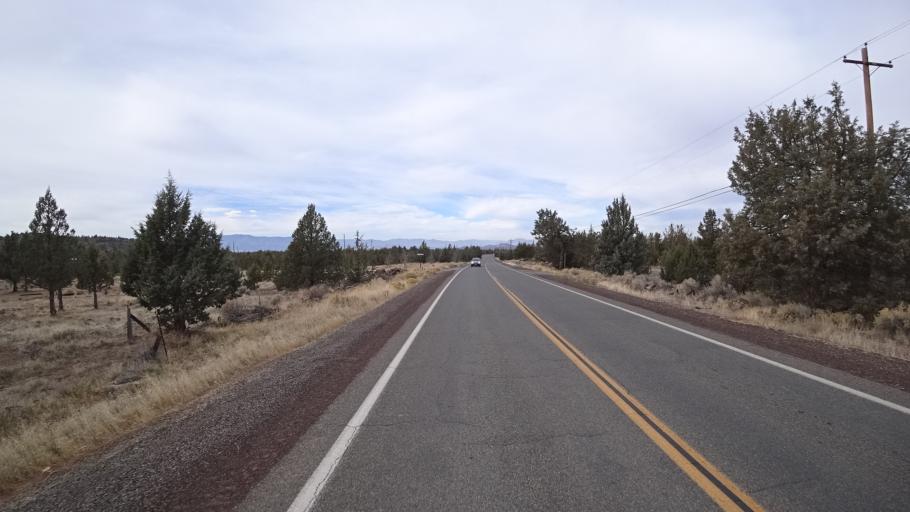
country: US
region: California
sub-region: Siskiyou County
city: Weed
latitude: 41.6053
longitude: -122.3593
